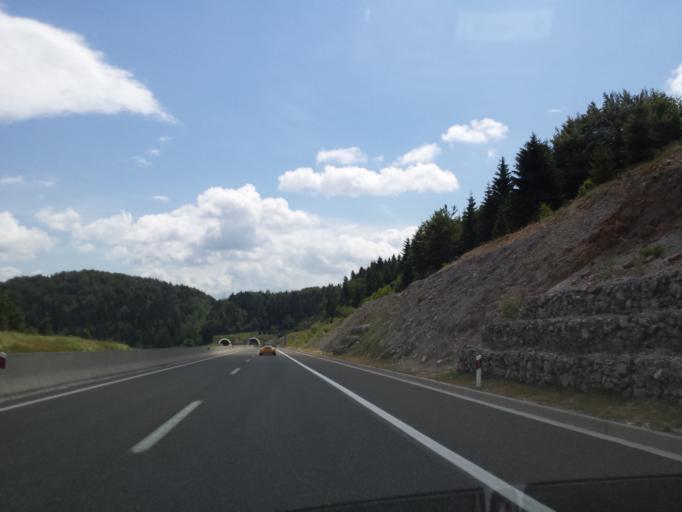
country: HR
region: Primorsko-Goranska
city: Vrbovsko
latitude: 45.3735
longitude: 15.0003
